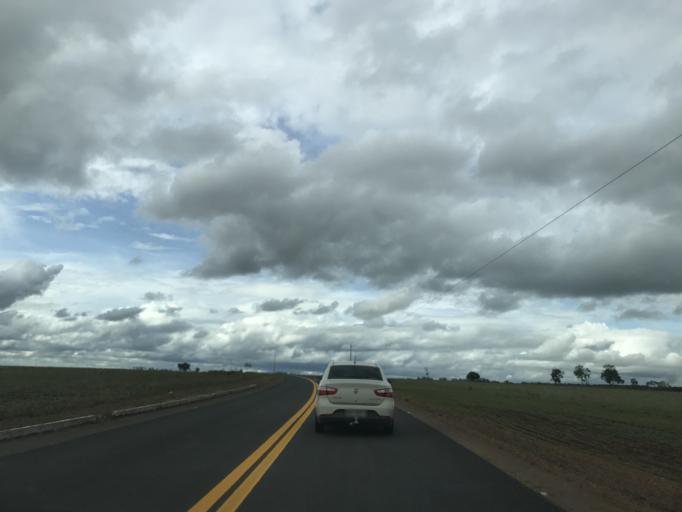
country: BR
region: Goias
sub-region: Bela Vista De Goias
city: Bela Vista de Goias
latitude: -17.0897
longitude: -48.6531
